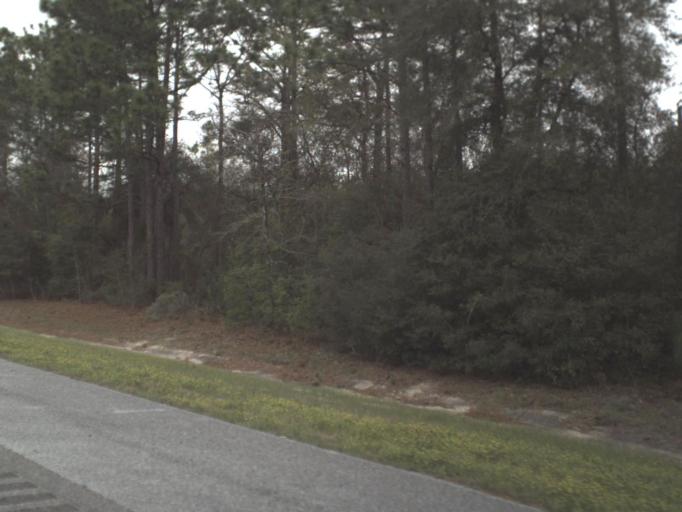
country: US
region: Florida
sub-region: Okaloosa County
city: Crestview
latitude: 30.7250
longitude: -86.4860
